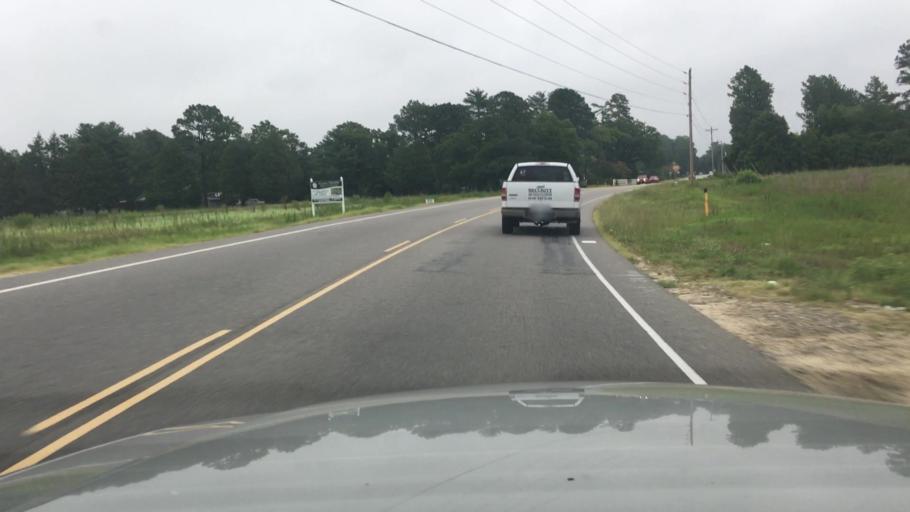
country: US
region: North Carolina
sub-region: Cumberland County
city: Hope Mills
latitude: 34.9753
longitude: -79.0008
